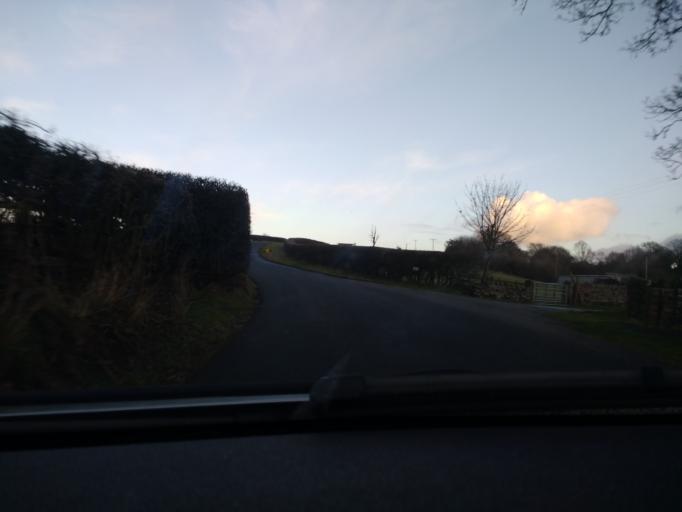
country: GB
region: England
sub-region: Cumbria
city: Carlisle
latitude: 54.7290
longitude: -2.9878
